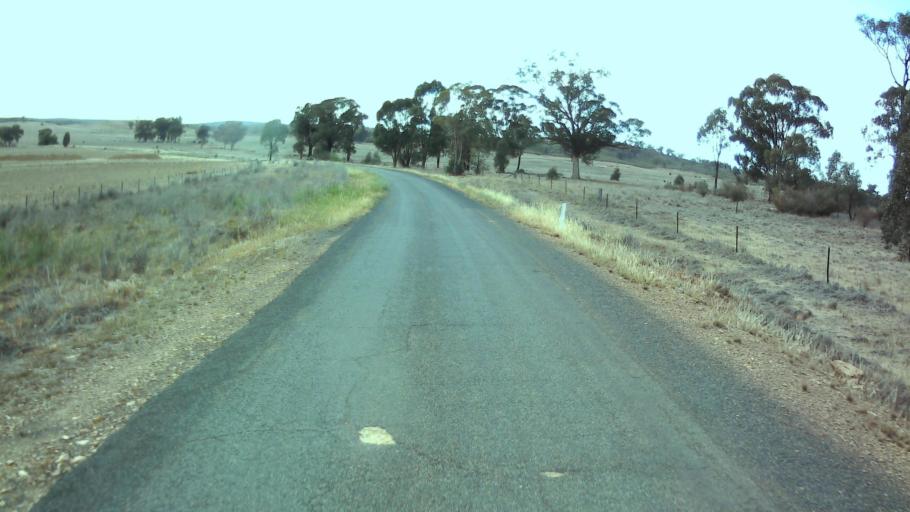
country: AU
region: New South Wales
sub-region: Weddin
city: Grenfell
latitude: -33.8450
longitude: 148.2432
